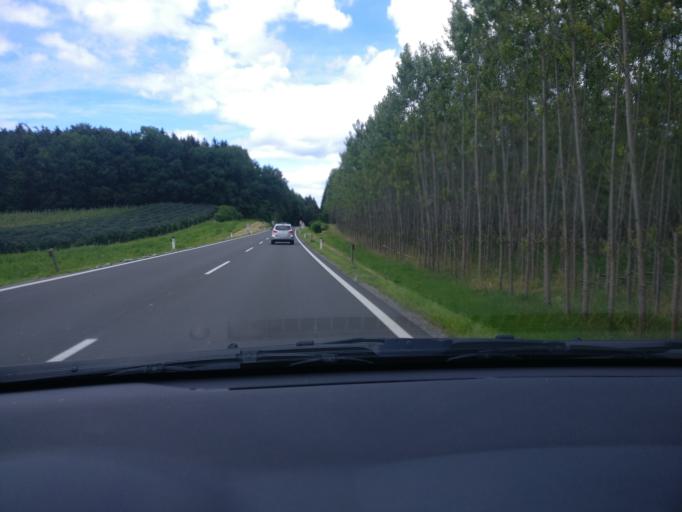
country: AT
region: Styria
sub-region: Politischer Bezirk Weiz
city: Oberrettenbach
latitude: 47.1536
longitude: 15.7704
